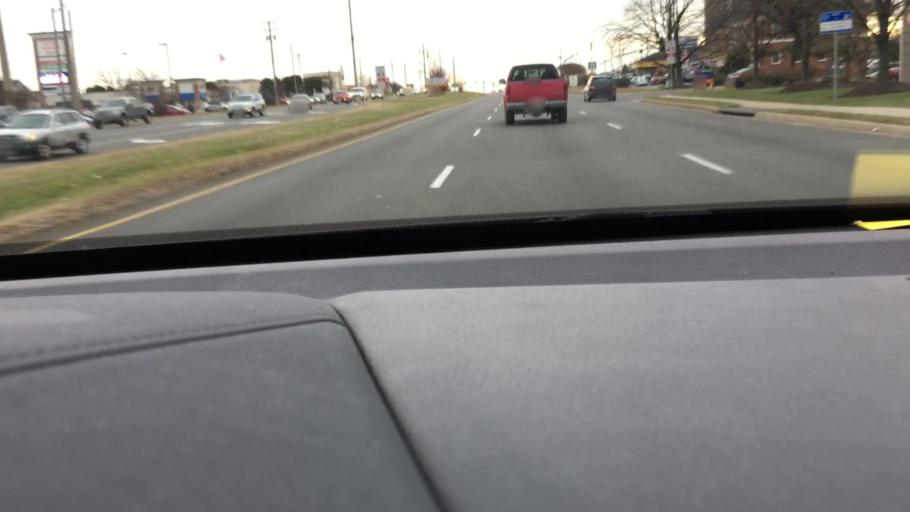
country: US
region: Virginia
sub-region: Prince William County
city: Bull Run
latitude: 38.7873
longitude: -77.5141
